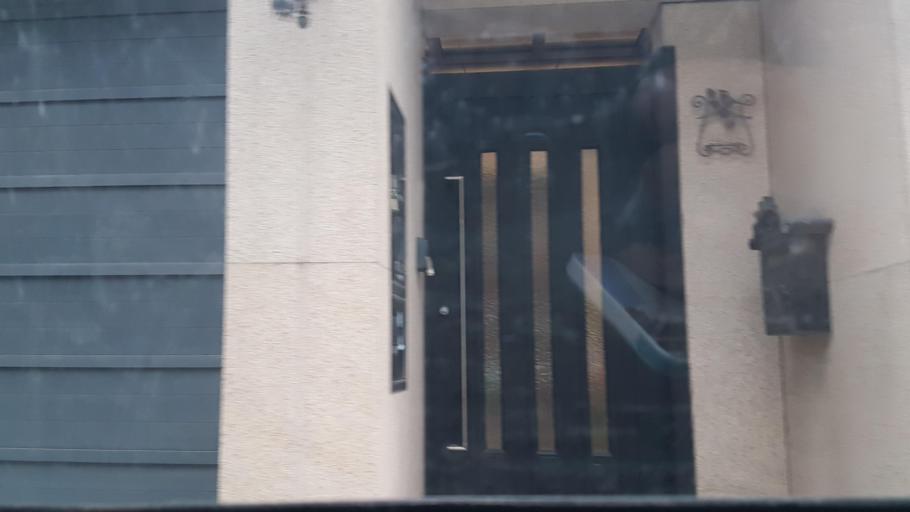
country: TW
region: Taiwan
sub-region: Hualien
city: Hualian
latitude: 23.9792
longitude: 121.5979
